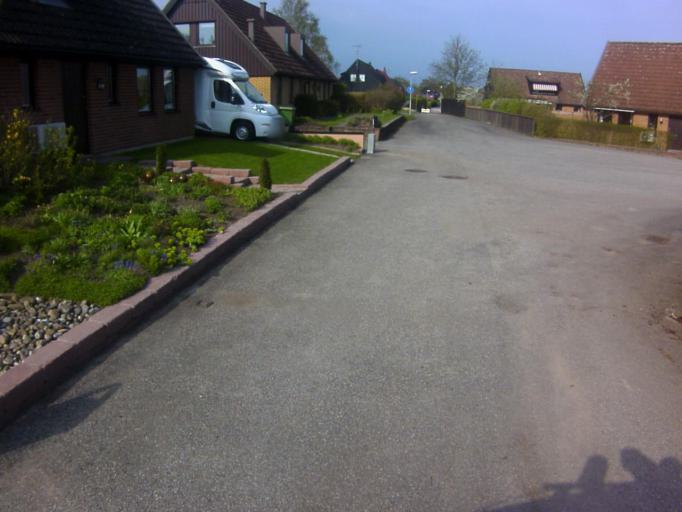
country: SE
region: Skane
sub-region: Kavlinge Kommun
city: Loddekopinge
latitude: 55.8190
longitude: 13.0366
